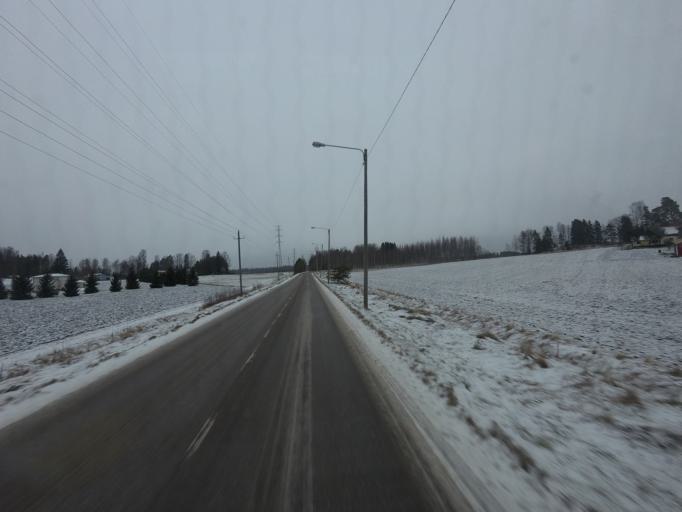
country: FI
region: Uusimaa
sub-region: Helsinki
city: Espoo
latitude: 60.1943
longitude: 24.5701
